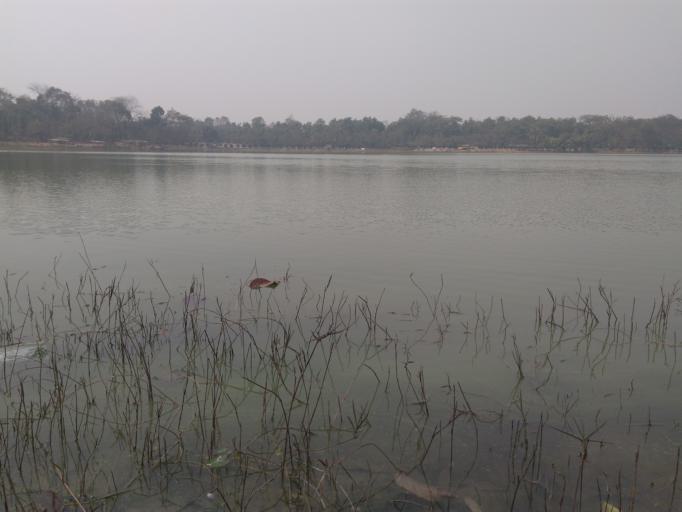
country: BD
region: Rangpur Division
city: Dinajpur
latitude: 25.5508
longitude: 88.6247
